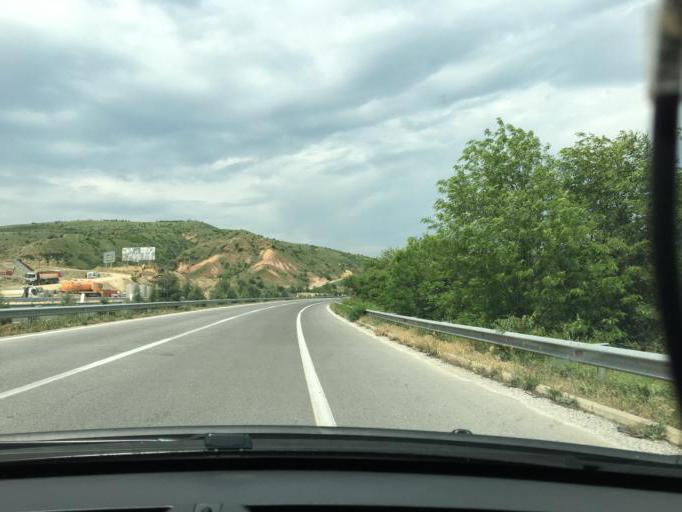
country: MK
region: Demir Kapija
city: Demir Kapija
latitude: 41.4261
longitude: 22.1866
